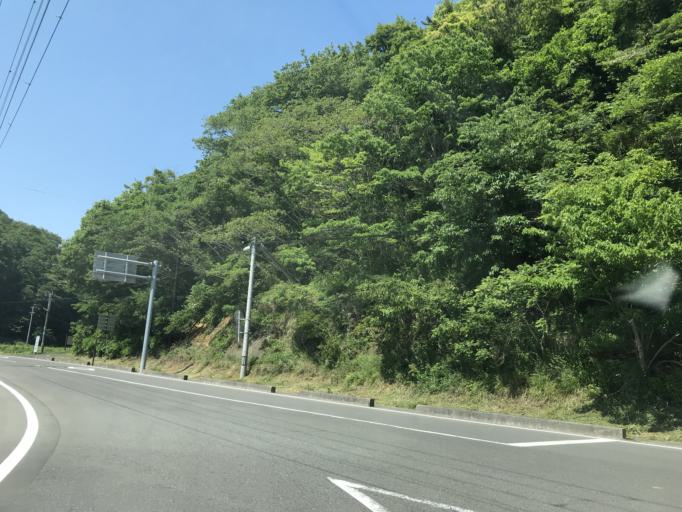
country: JP
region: Miyagi
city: Matsushima
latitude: 38.3325
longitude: 141.1582
